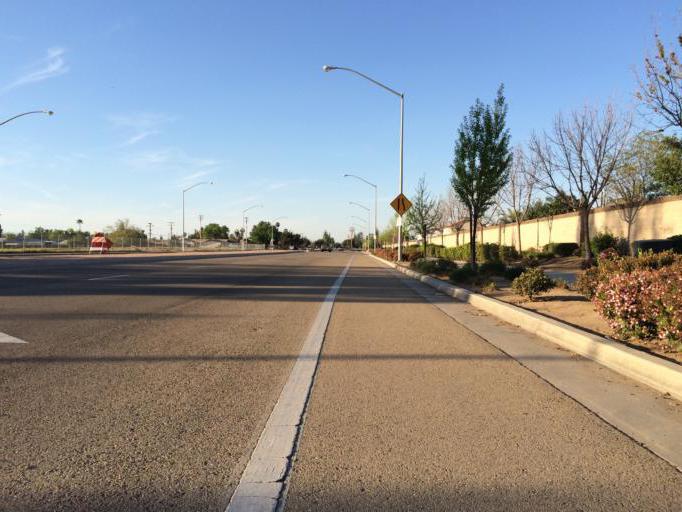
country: US
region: California
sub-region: Fresno County
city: Tarpey Village
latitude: 36.7804
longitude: -119.6821
